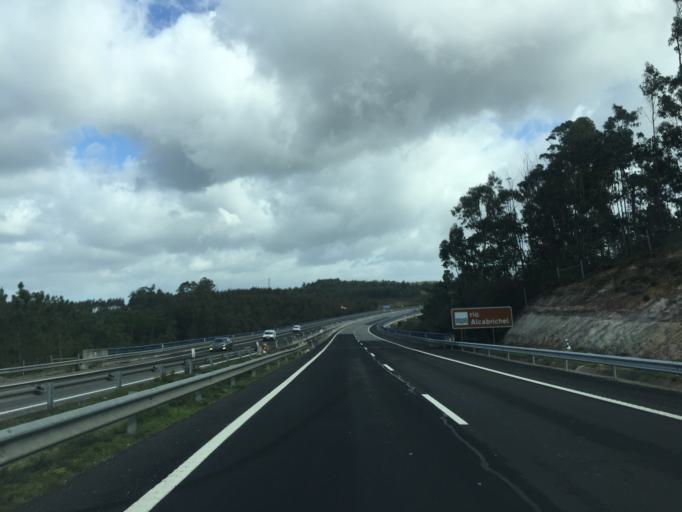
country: PT
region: Lisbon
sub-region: Torres Vedras
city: A dos Cunhados
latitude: 39.1455
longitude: -9.2446
